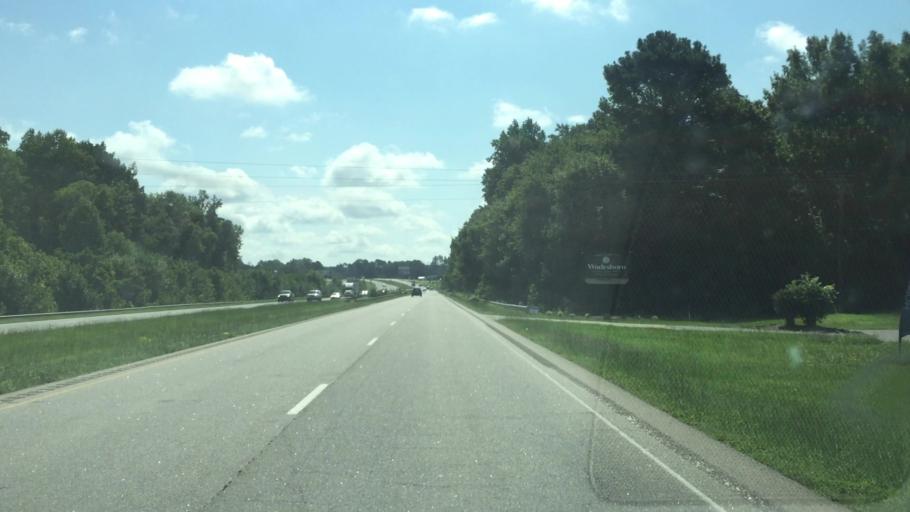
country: US
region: North Carolina
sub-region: Anson County
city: Wadesboro
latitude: 34.9805
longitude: -80.1264
